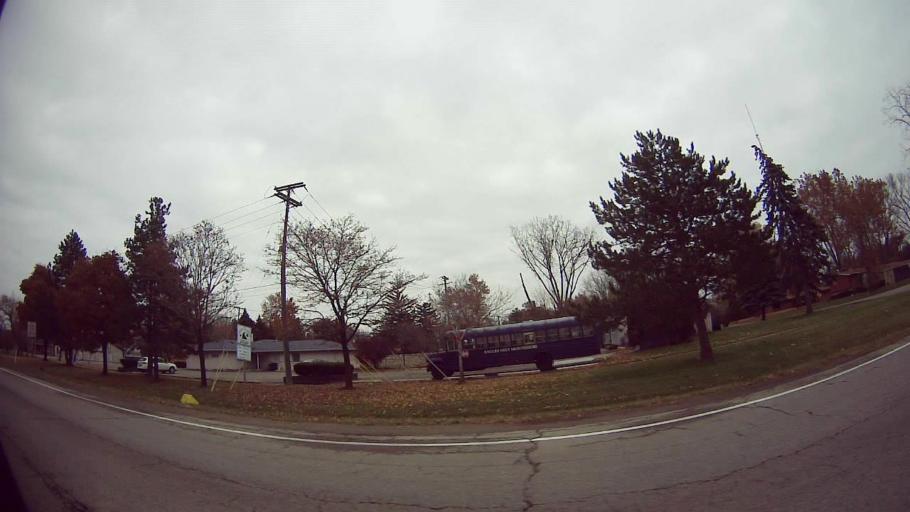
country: US
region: Michigan
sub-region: Oakland County
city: Southfield
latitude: 42.4638
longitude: -83.2206
